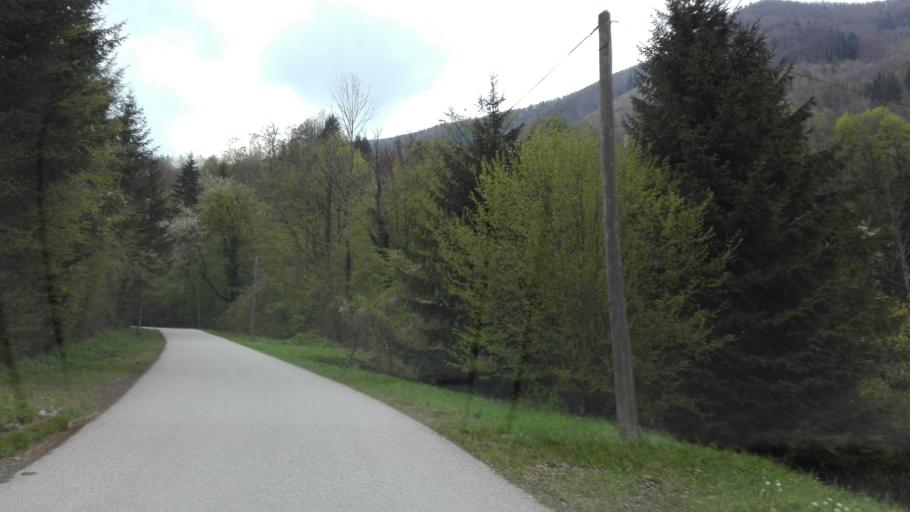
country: AT
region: Upper Austria
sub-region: Politischer Bezirk Steyr-Land
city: Ternberg
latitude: 47.9186
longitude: 14.3290
